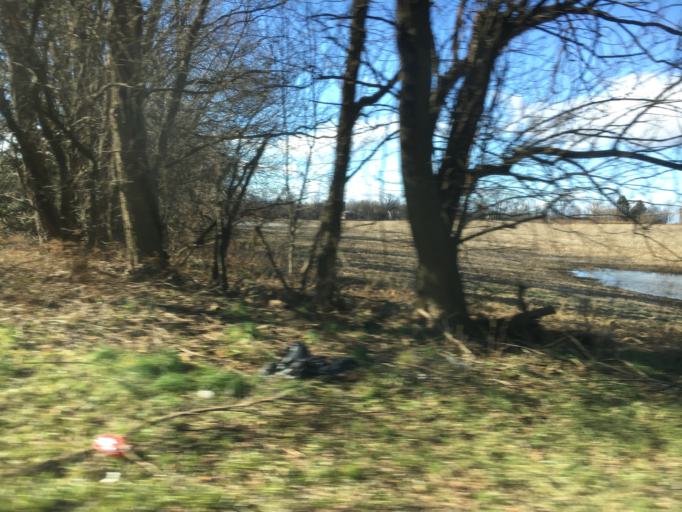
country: US
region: Pennsylvania
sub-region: Lehigh County
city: Egypt
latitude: 40.6448
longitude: -75.5475
